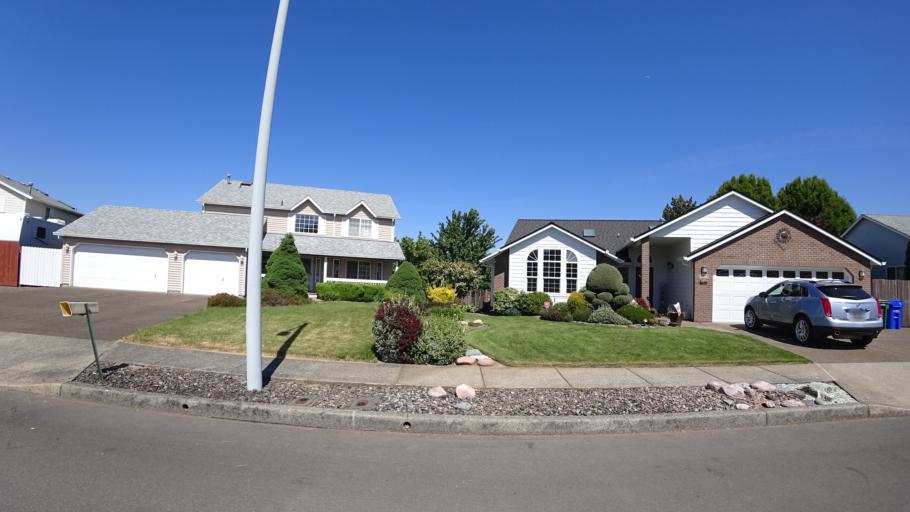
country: US
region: Oregon
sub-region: Multnomah County
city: Gresham
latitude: 45.4787
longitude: -122.4729
